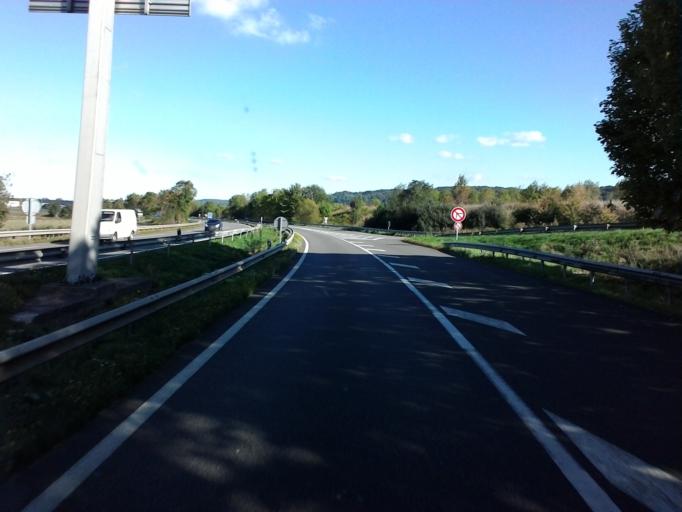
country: FR
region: Lorraine
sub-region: Departement de Meurthe-et-Moselle
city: Mont-Saint-Martin
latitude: 49.5477
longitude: 5.7990
